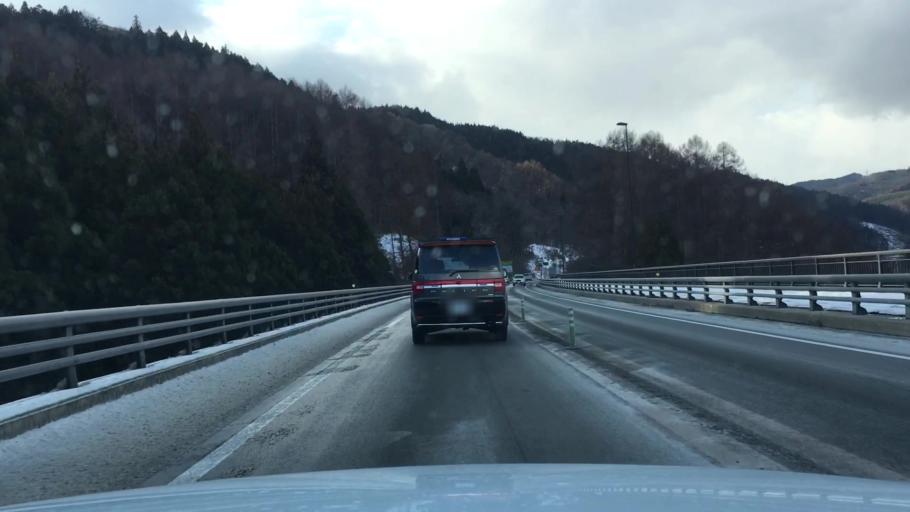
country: JP
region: Iwate
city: Morioka-shi
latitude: 39.6673
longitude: 141.2394
